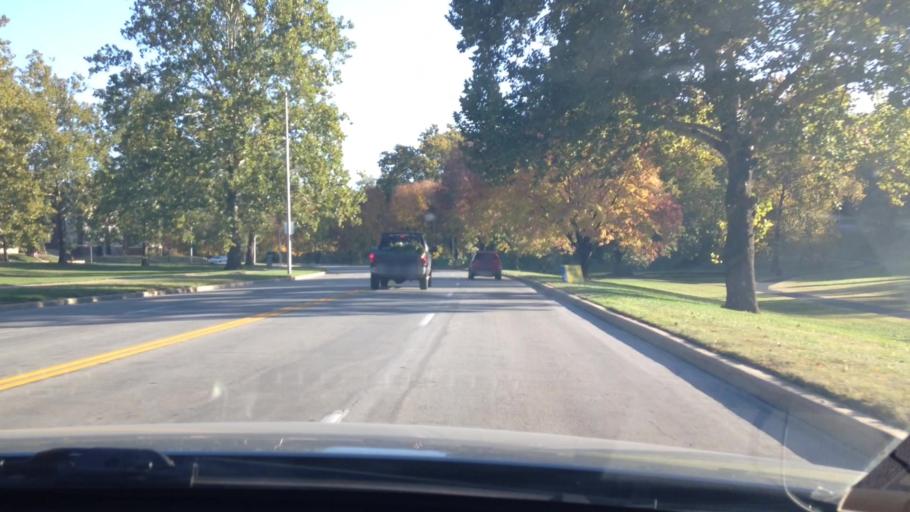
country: US
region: Kansas
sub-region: Johnson County
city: Westwood
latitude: 39.0502
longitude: -94.5792
